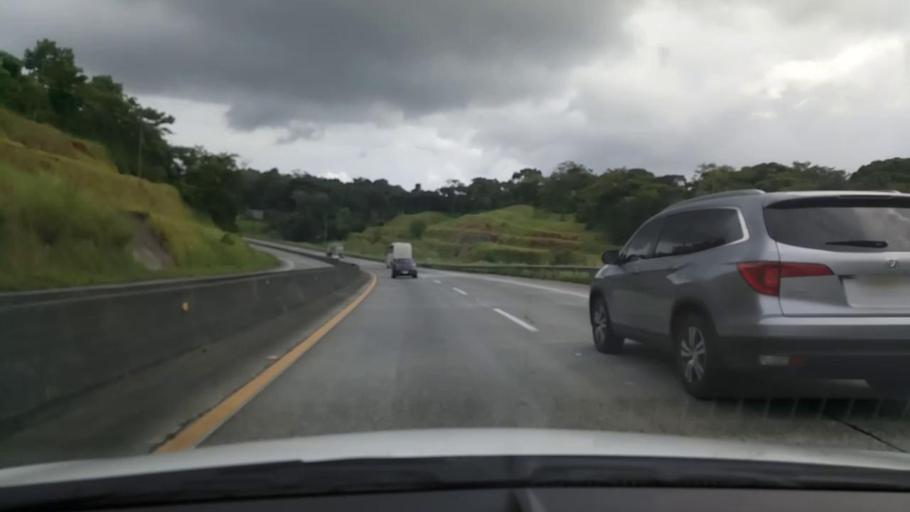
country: PA
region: Colon
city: Gatun
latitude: 9.2860
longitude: -79.7785
